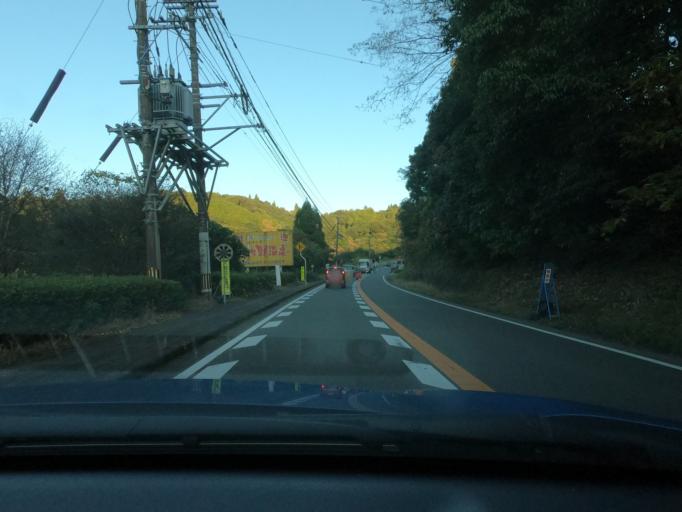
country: JP
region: Kagoshima
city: Satsumasendai
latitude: 31.8136
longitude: 130.3731
